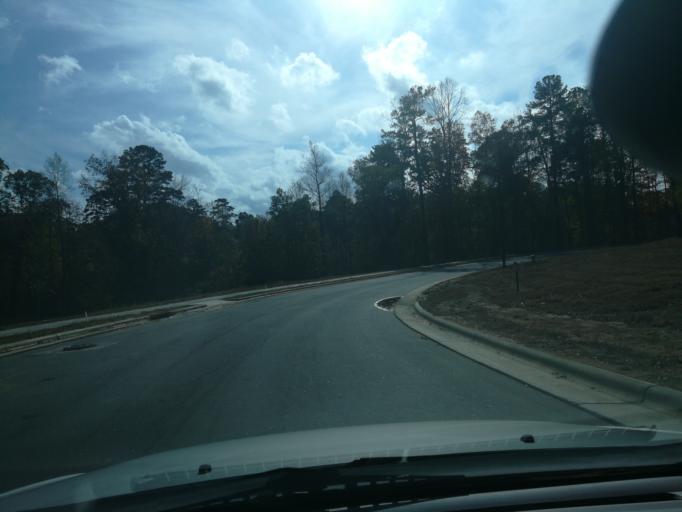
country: US
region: North Carolina
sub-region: Durham County
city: Durham
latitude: 36.0580
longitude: -78.9437
